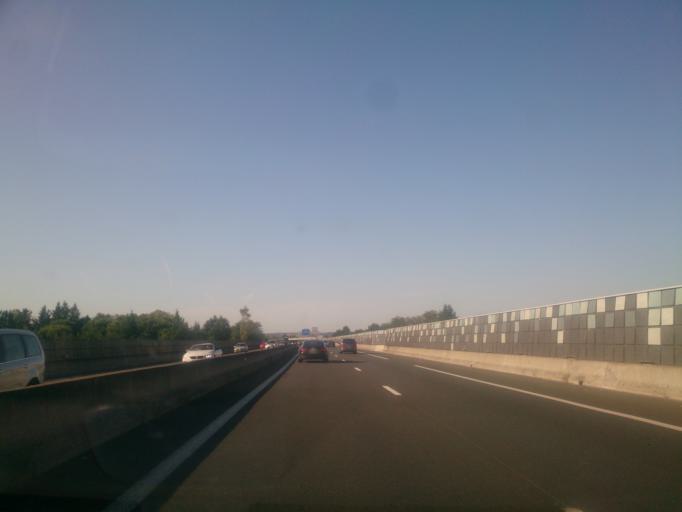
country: FR
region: Midi-Pyrenees
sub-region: Departement du Tarn-et-Garonne
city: Montauban
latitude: 44.0254
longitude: 1.3876
